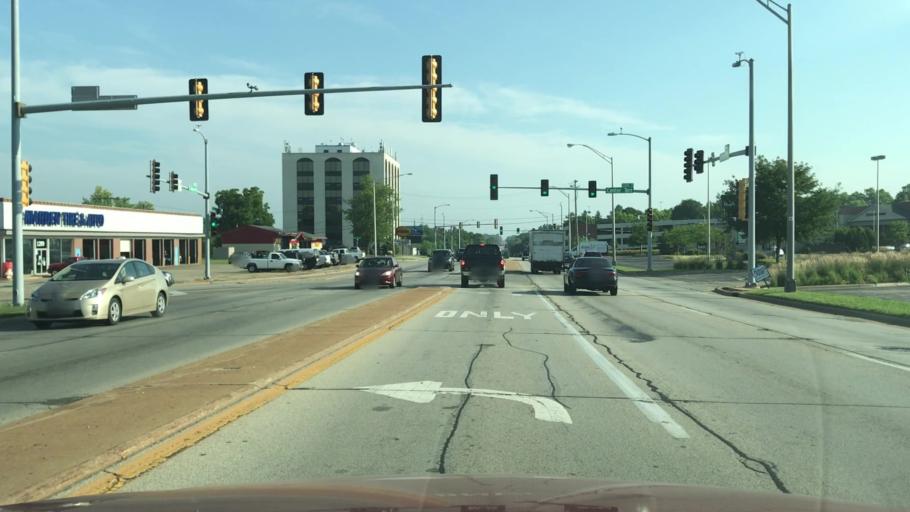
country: US
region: Illinois
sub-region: Winnebago County
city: Rockford
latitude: 42.2537
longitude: -89.0290
